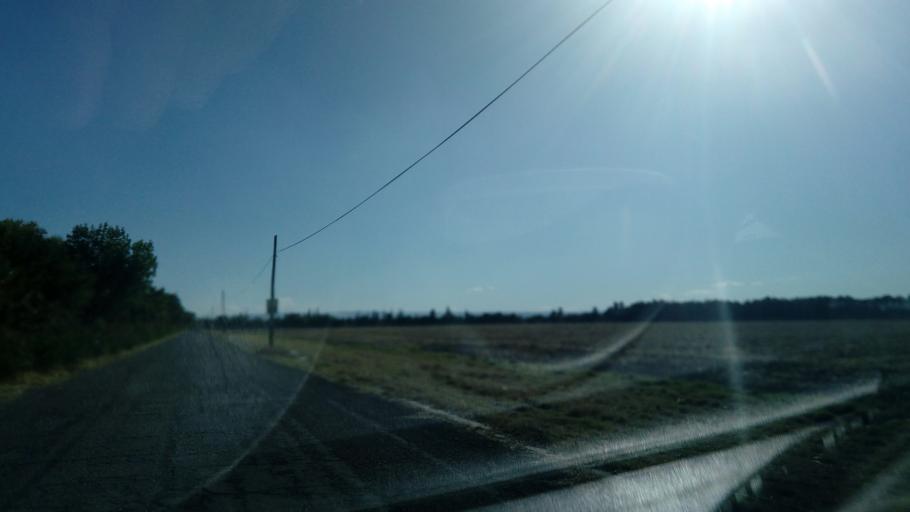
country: MX
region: Durango
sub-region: Durango
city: Jose Refugio Salcido
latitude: 24.0083
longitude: -104.5489
